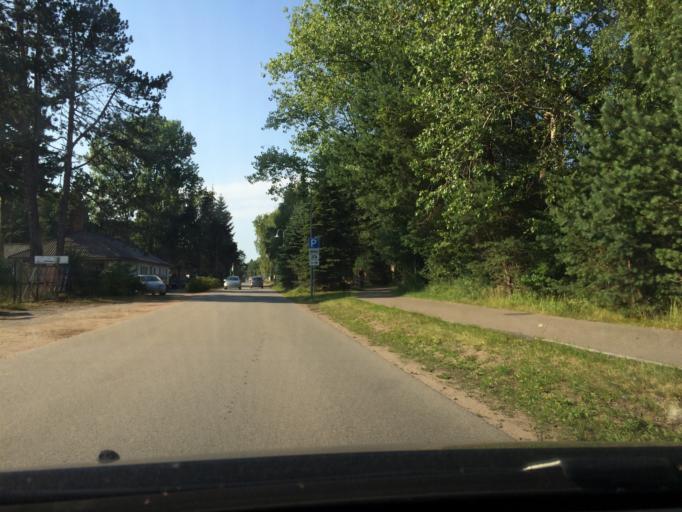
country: DE
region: Mecklenburg-Vorpommern
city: Ostseebad Binz
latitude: 54.4394
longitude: 13.5681
